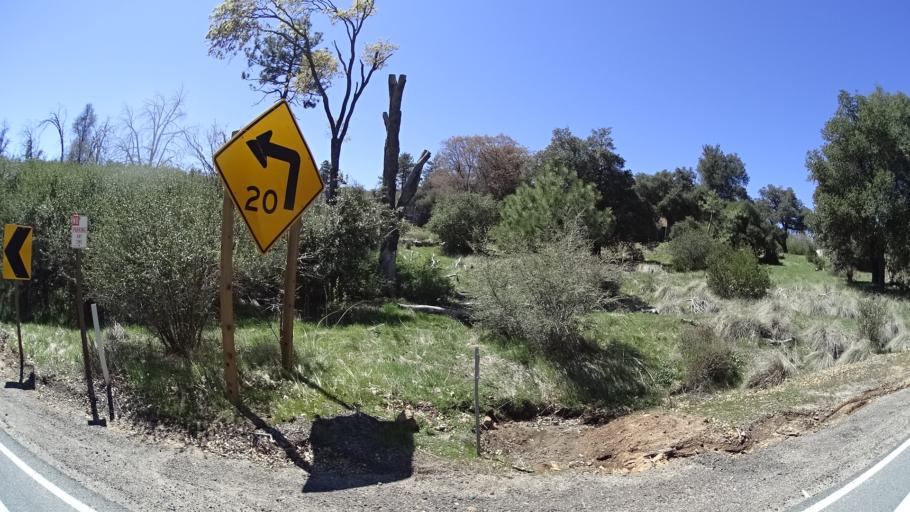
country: US
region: California
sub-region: San Diego County
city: Descanso
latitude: 32.9577
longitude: -116.5792
